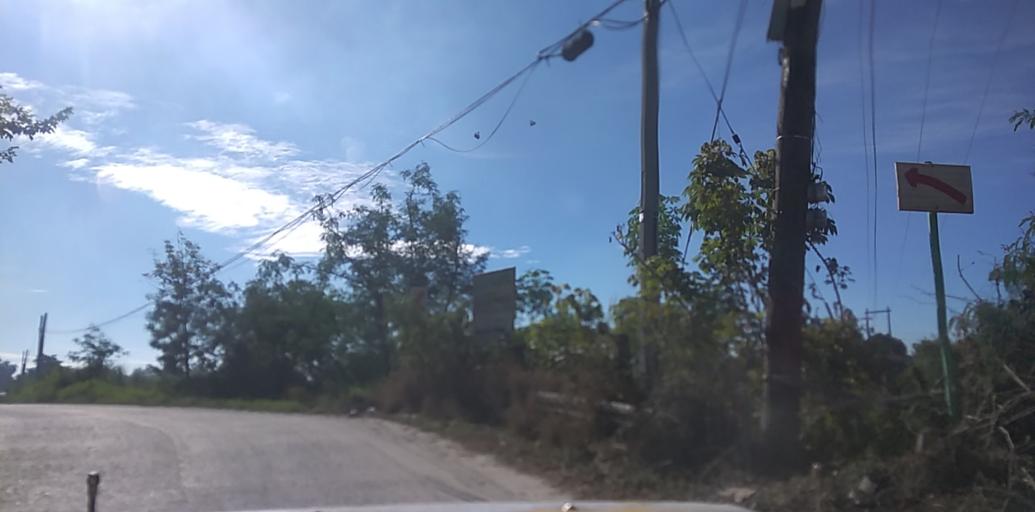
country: PH
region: Central Luzon
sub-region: Province of Pampanga
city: Anao
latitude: 15.1209
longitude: 120.7012
